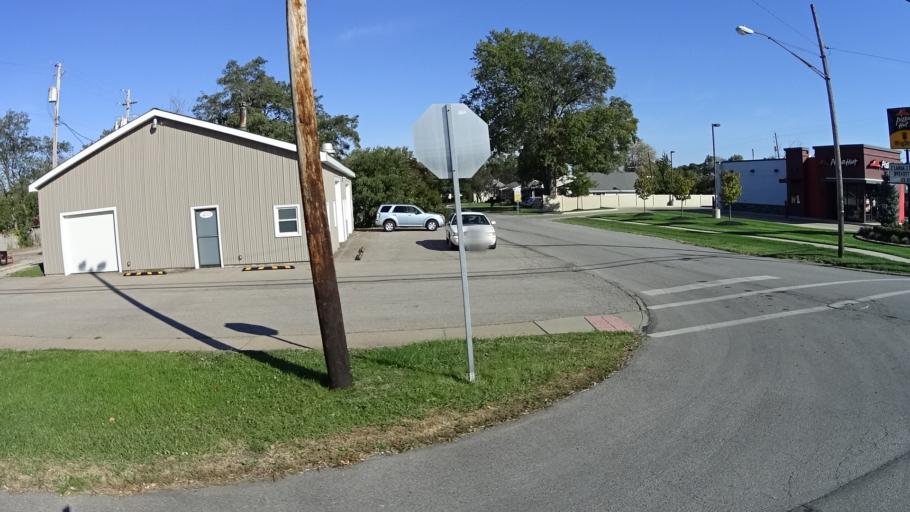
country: US
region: Ohio
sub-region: Lorain County
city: Vermilion-on-the-Lake
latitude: 41.4250
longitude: -82.3381
